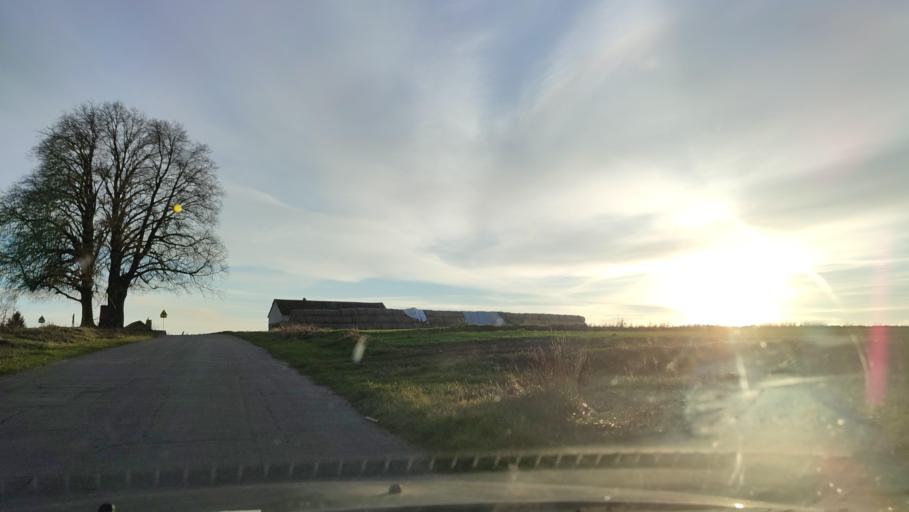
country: PL
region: Masovian Voivodeship
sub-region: Powiat mlawski
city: Dzierzgowo
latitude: 53.2715
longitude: 20.6453
